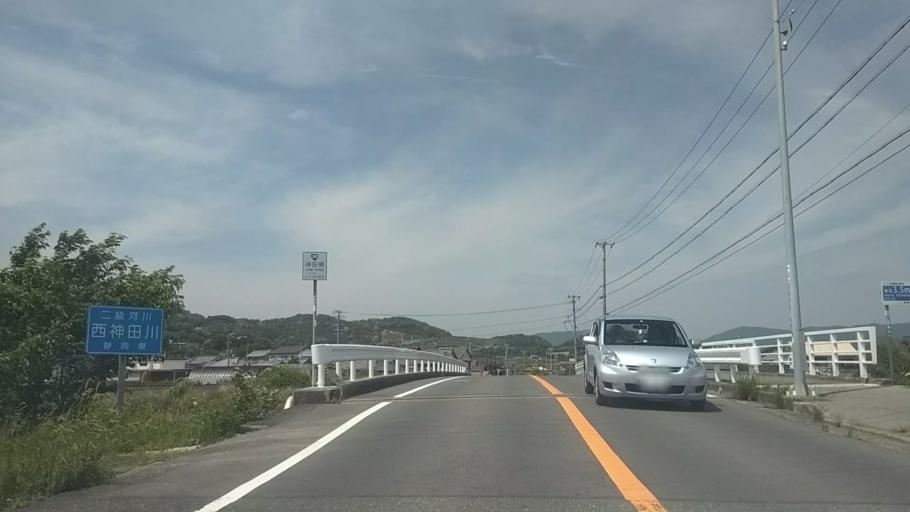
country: JP
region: Shizuoka
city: Kosai-shi
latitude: 34.7814
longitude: 137.5415
